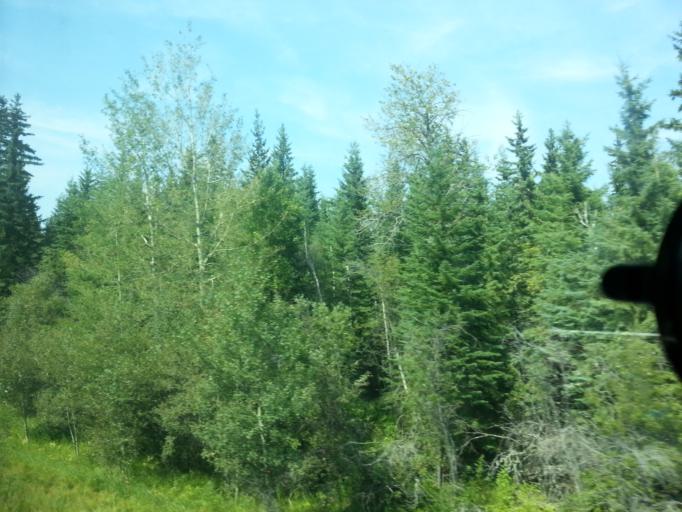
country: CA
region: Alberta
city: Mayerthorpe
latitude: 53.6051
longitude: -115.2890
